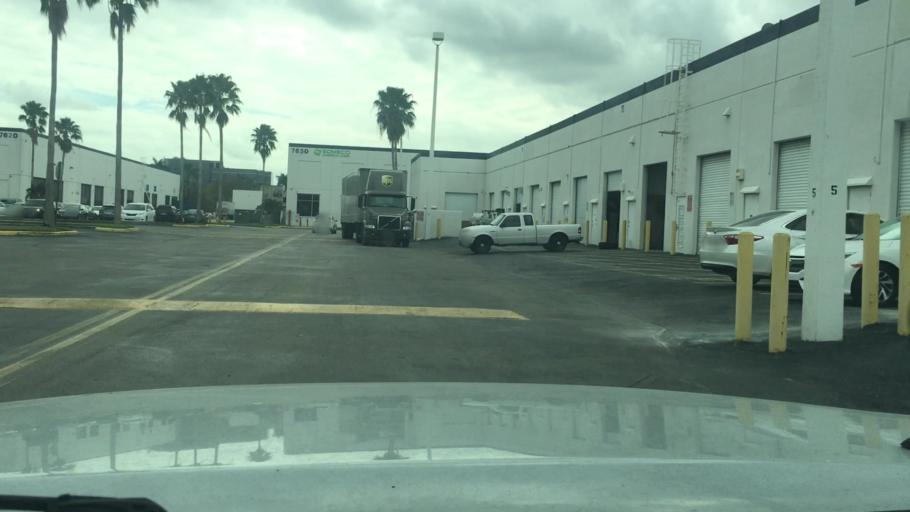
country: US
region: Florida
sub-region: Miami-Dade County
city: Virginia Gardens
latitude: 25.7952
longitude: -80.3201
